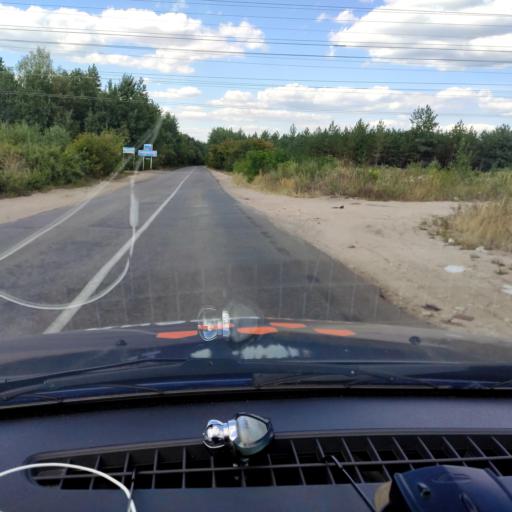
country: RU
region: Voronezj
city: Somovo
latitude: 51.7111
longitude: 39.3677
